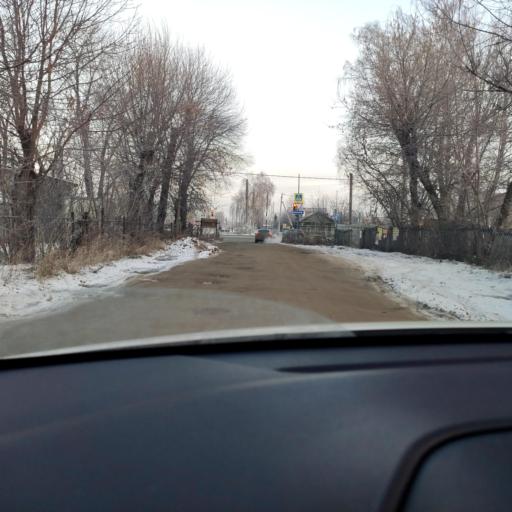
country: RU
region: Tatarstan
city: Staroye Arakchino
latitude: 55.8655
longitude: 49.0469
